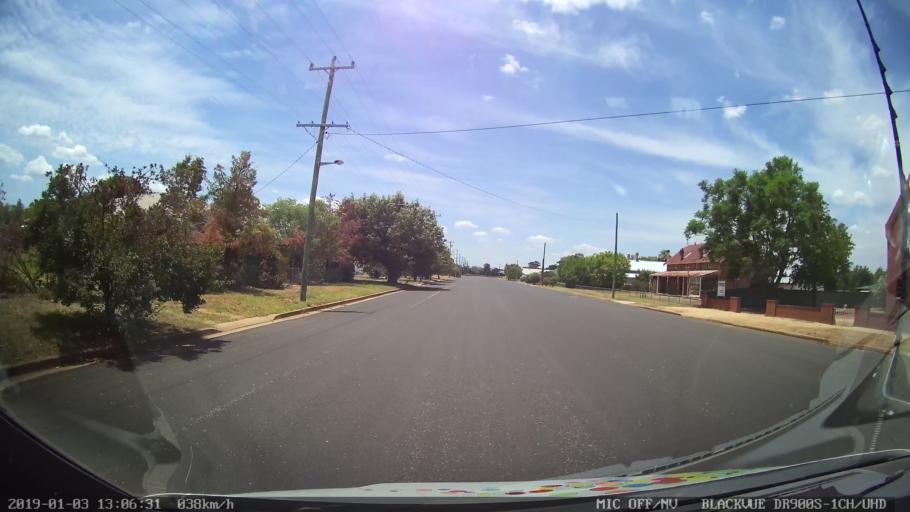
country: AU
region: New South Wales
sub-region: Cabonne
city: Canowindra
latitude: -33.6148
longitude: 148.4314
